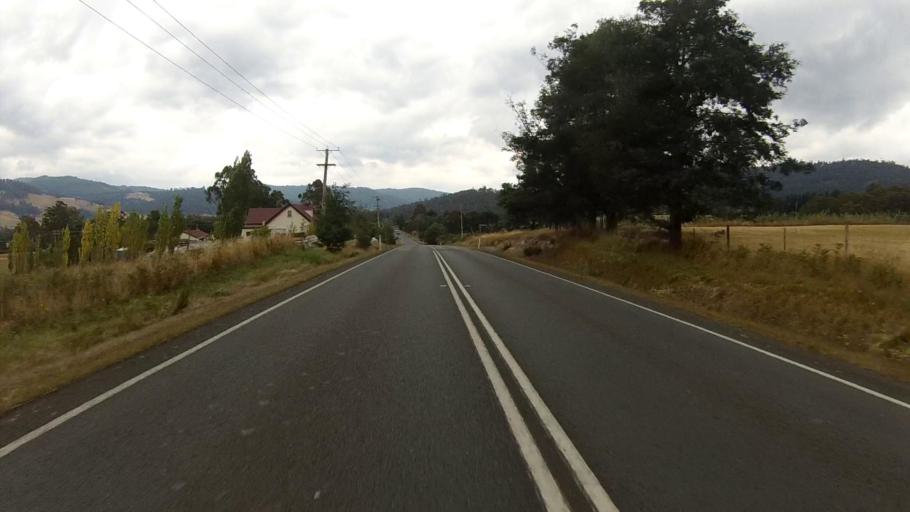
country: AU
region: Tasmania
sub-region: Huon Valley
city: Franklin
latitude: -43.1103
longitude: 147.0359
